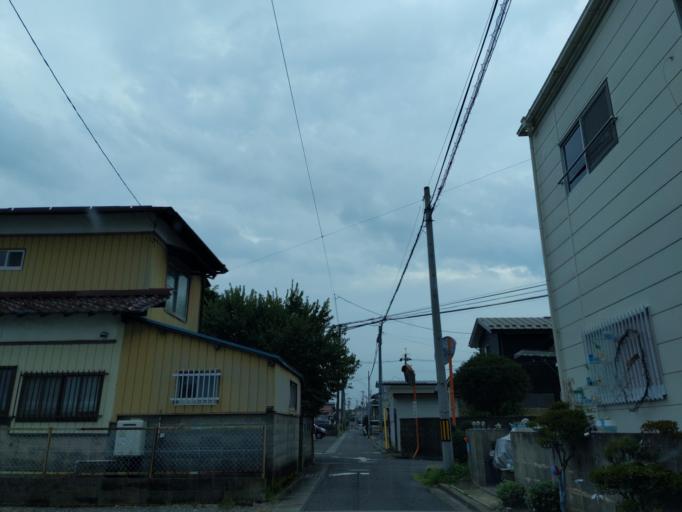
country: JP
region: Fukushima
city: Koriyama
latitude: 37.3952
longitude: 140.3453
